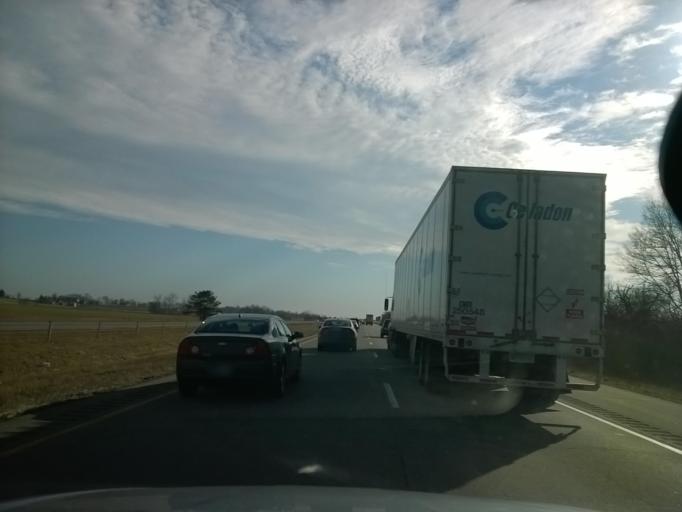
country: US
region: Indiana
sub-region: Johnson County
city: Edinburgh
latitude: 39.3745
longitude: -85.9428
